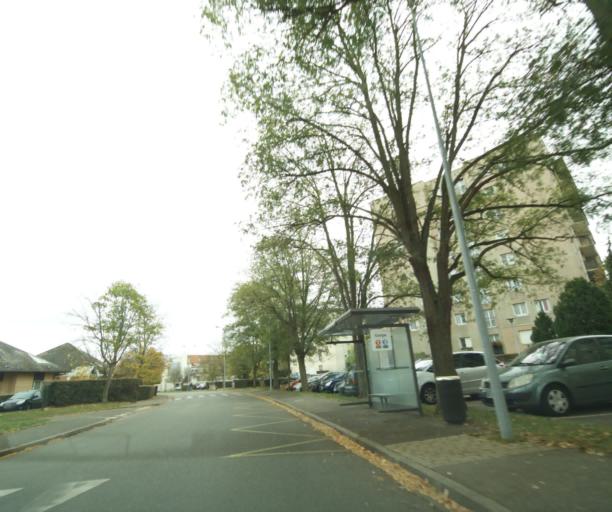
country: FR
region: Centre
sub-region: Departement d'Eure-et-Loir
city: Dreux
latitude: 48.7393
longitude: 1.3475
